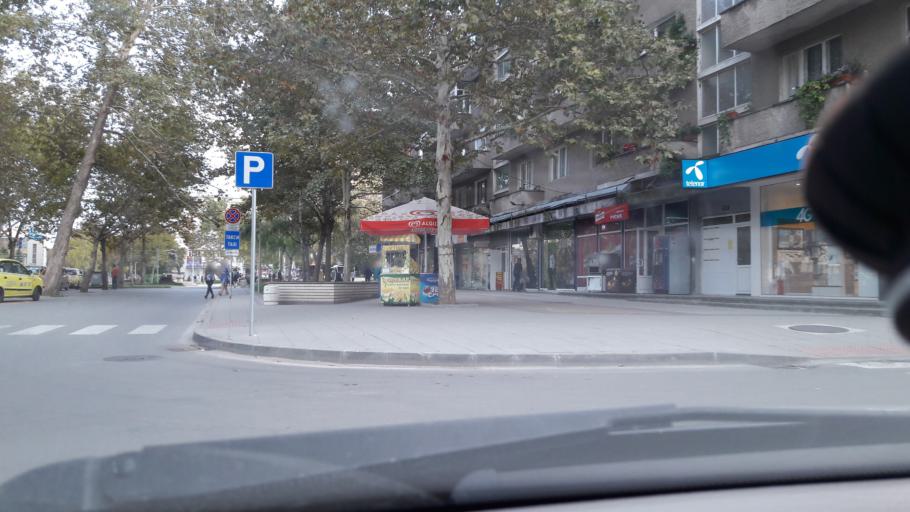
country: BG
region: Razgrad
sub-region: Obshtina Razgrad
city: Razgrad
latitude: 43.5253
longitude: 26.5220
